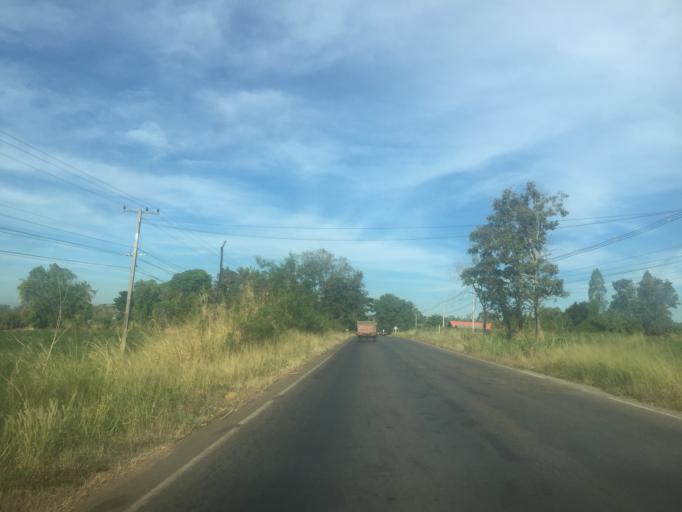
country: TH
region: Kalasin
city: Tha Khantho
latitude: 16.9649
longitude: 103.2466
